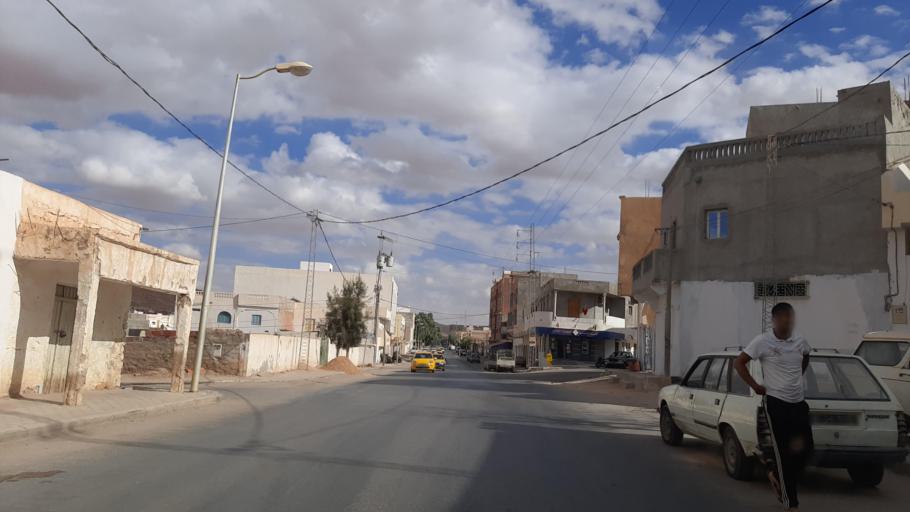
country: TN
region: Tataouine
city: Tataouine
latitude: 32.9238
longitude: 10.4571
